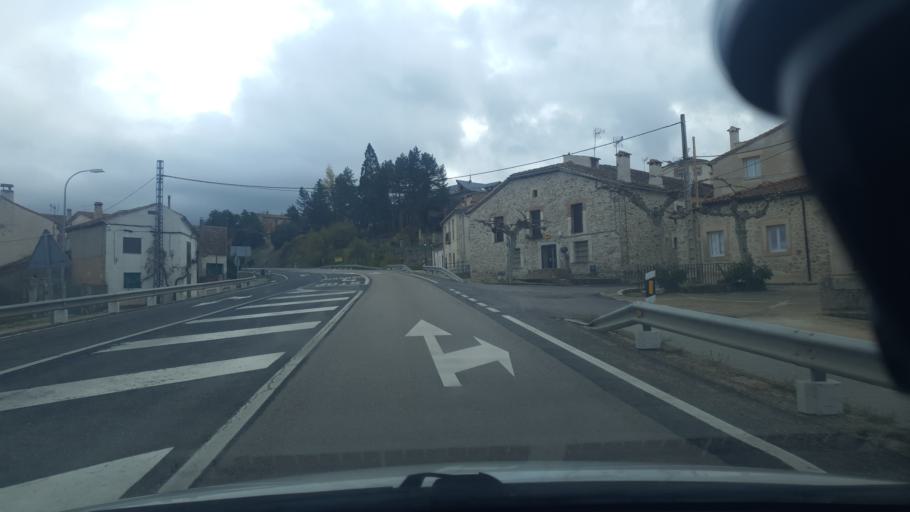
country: ES
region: Castille and Leon
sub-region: Provincia de Segovia
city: Cerezo de Abajo
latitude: 41.2180
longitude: -3.5906
